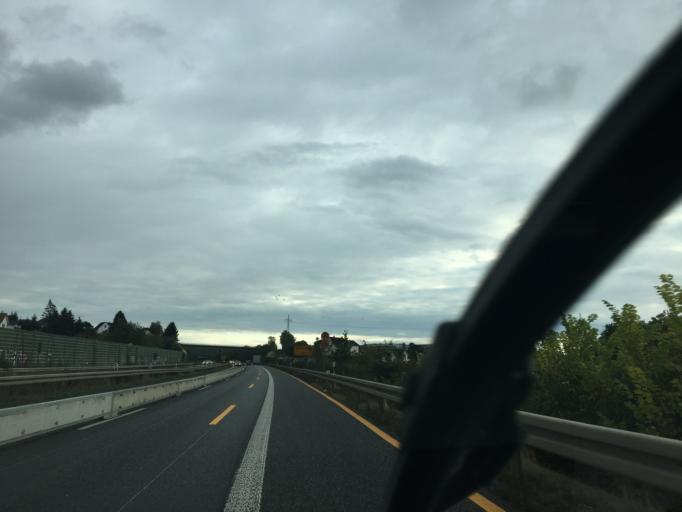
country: DE
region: Hesse
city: Staufenberg
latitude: 50.6624
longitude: 8.7207
